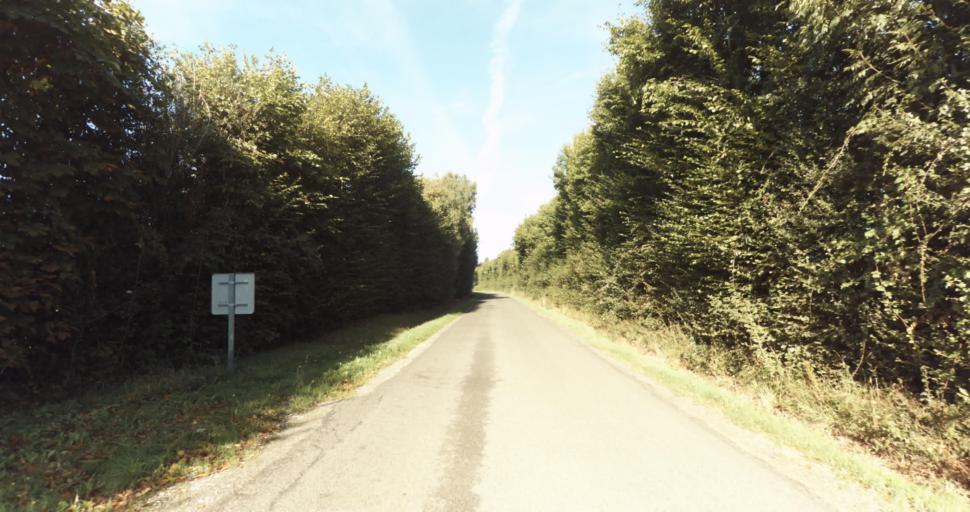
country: FR
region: Lower Normandy
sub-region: Departement de l'Orne
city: Vimoutiers
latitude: 48.9291
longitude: 0.2866
